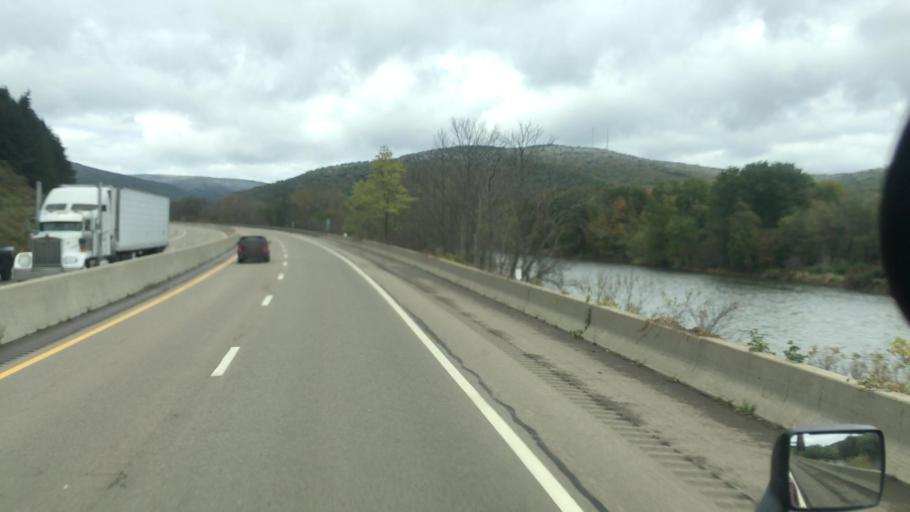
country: US
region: New York
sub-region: Cattaraugus County
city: Salamanca
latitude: 42.1417
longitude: -78.6665
